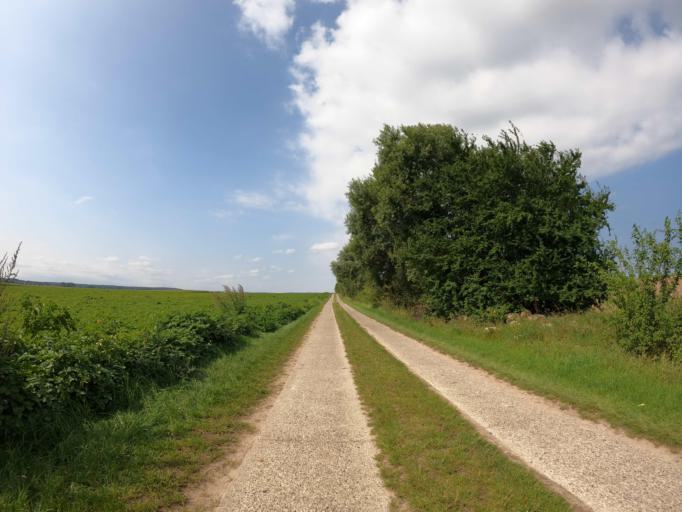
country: DE
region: Mecklenburg-Vorpommern
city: Malchow
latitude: 53.4351
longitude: 12.4961
